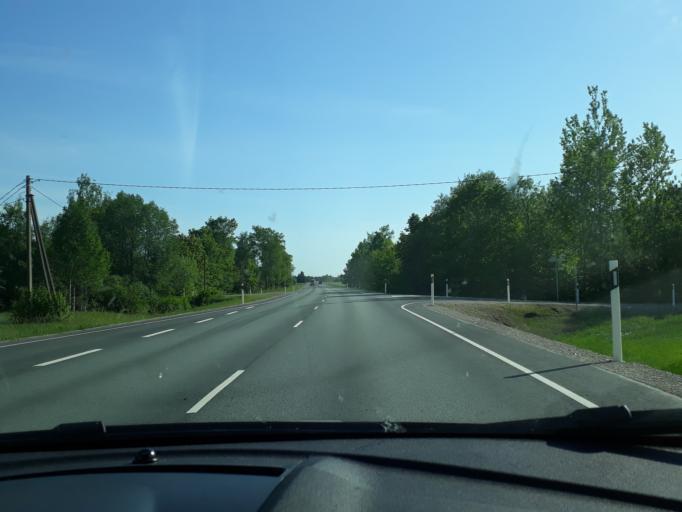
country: EE
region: Paernumaa
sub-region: Tootsi vald
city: Tootsi
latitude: 58.5361
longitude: 24.8347
